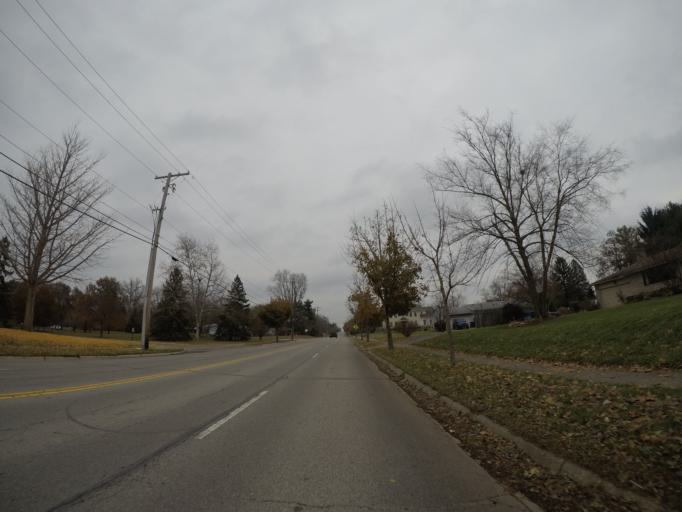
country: US
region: Ohio
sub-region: Franklin County
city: Upper Arlington
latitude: 40.0408
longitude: -83.0721
